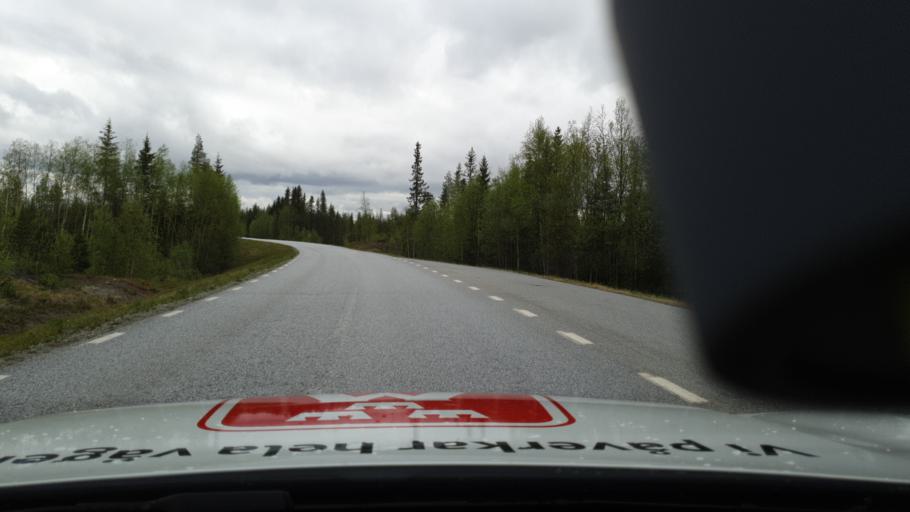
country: SE
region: Vaesterbotten
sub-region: Vilhelmina Kommun
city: Sjoberg
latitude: 64.8092
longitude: 15.9786
